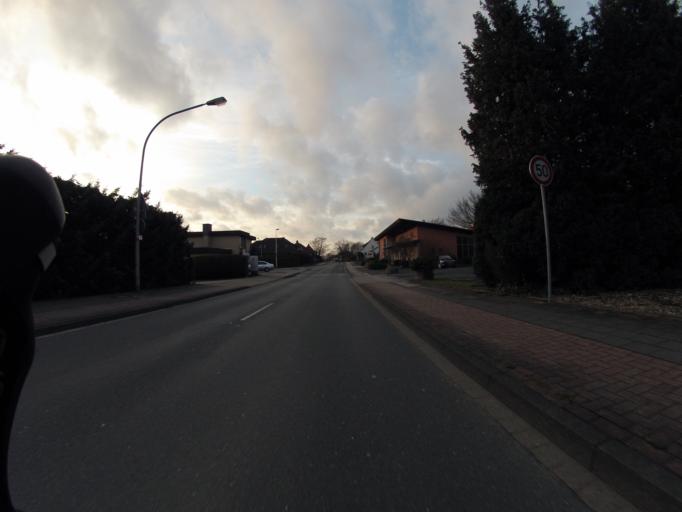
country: DE
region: North Rhine-Westphalia
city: Ibbenburen
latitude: 52.2700
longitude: 7.7408
